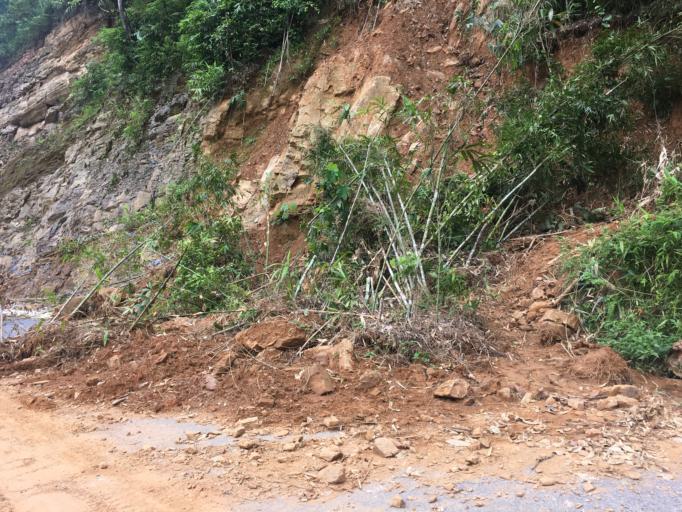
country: VN
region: Ha Giang
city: Thi Tran Tam Son
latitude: 22.9519
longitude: 105.0381
